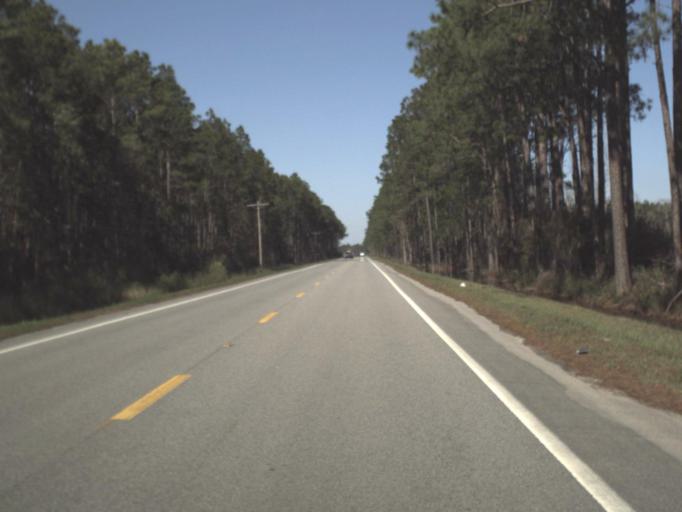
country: US
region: Florida
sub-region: Gulf County
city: Wewahitchka
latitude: 29.9618
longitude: -85.1751
